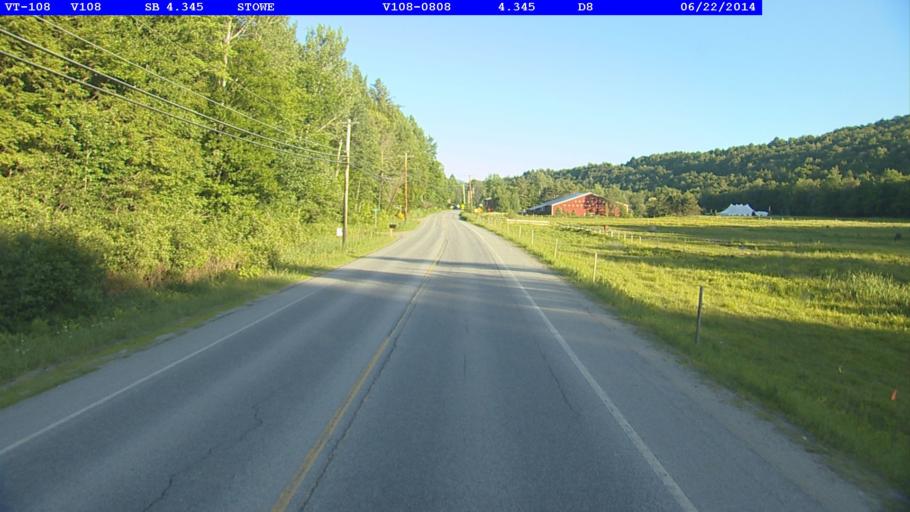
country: US
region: Vermont
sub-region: Lamoille County
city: Morristown
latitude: 44.4975
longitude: -72.7434
